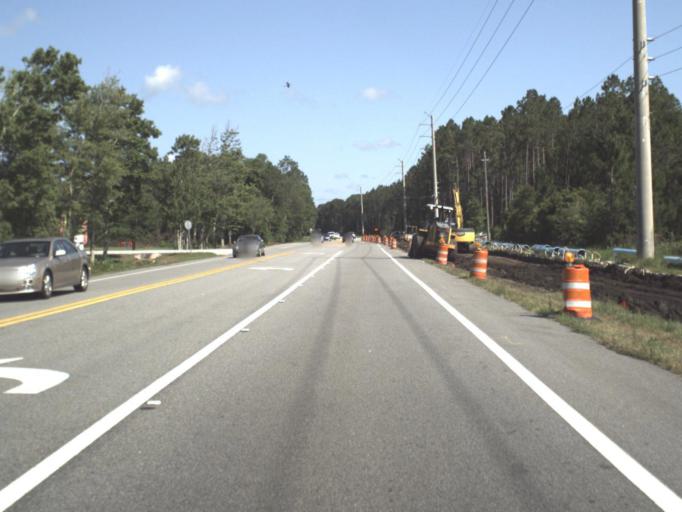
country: US
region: Florida
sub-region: Saint Johns County
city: Saint Augustine
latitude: 29.9384
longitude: -81.4371
